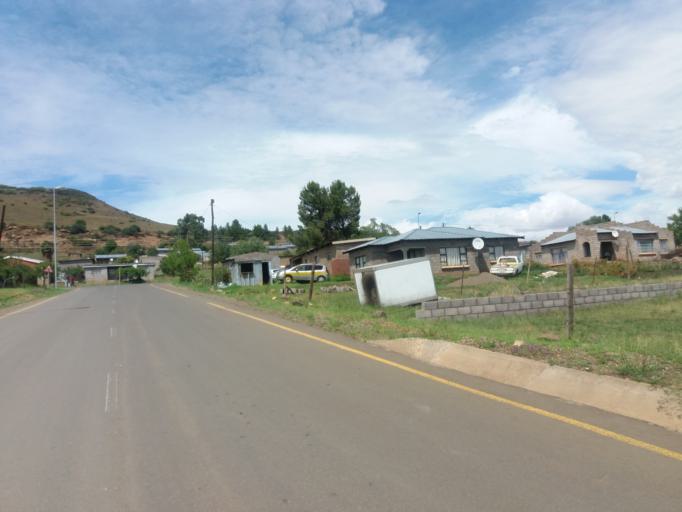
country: LS
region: Quthing
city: Quthing
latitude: -30.4103
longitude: 27.6959
